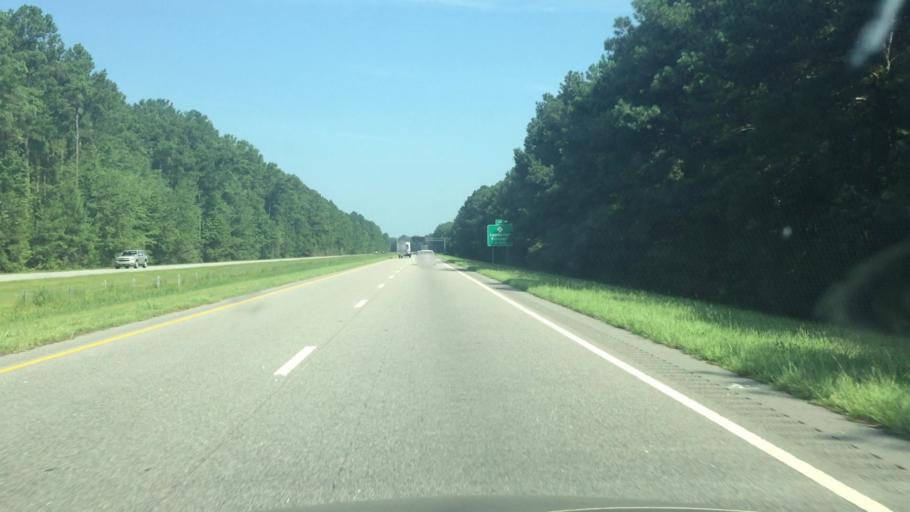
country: US
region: North Carolina
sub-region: Robeson County
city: Lumberton
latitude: 34.5544
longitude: -79.0246
